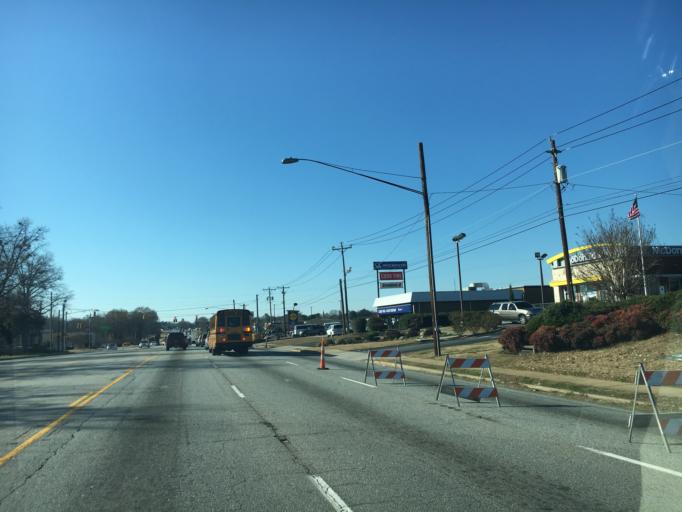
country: US
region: South Carolina
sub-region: Greenville County
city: Wade Hampton
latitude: 34.8857
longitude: -82.3533
